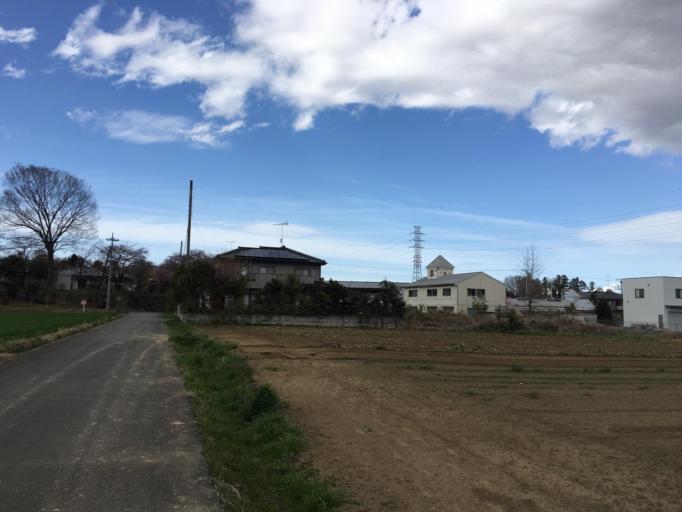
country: JP
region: Saitama
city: Ogawa
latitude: 36.1124
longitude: 139.2568
